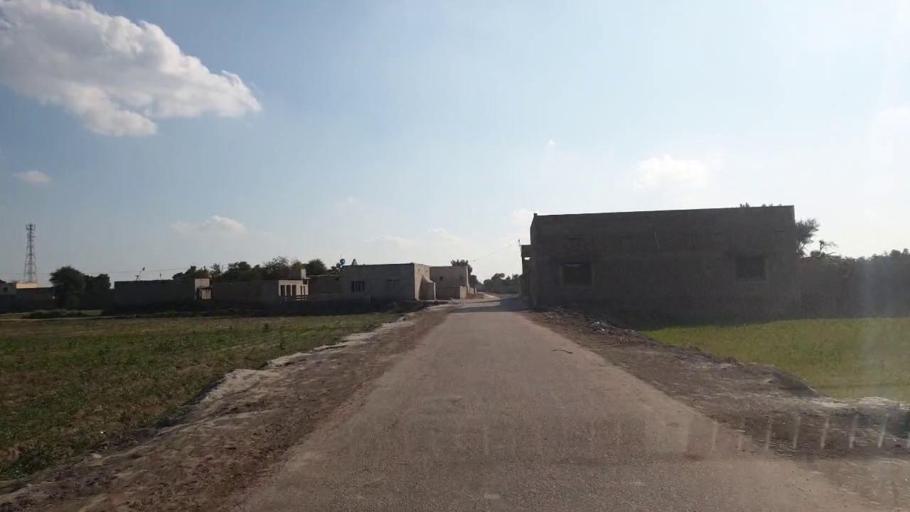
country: PK
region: Sindh
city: Shahpur Chakar
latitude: 26.1060
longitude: 68.5645
